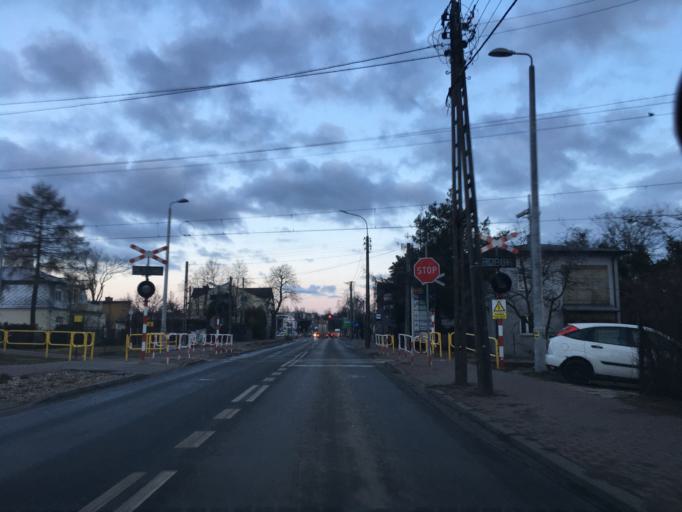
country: PL
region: Masovian Voivodeship
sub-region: Powiat grodziski
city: Grodzisk Mazowiecki
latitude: 52.1032
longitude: 20.6371
